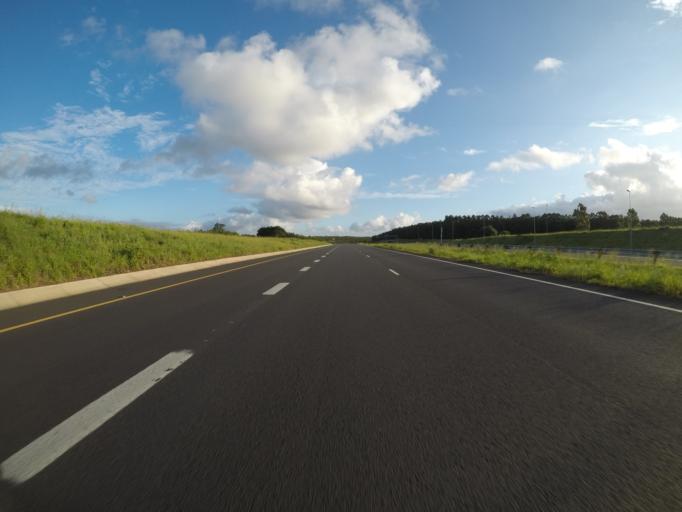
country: ZA
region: KwaZulu-Natal
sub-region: uThungulu District Municipality
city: KwaMbonambi
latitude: -28.5199
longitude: 32.1381
